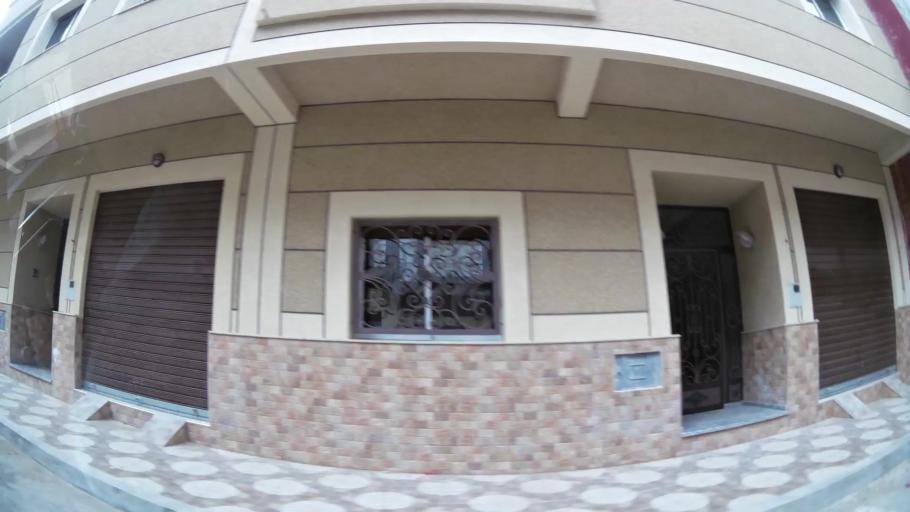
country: MA
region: Oriental
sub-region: Nador
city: Nador
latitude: 35.1610
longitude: -2.9387
